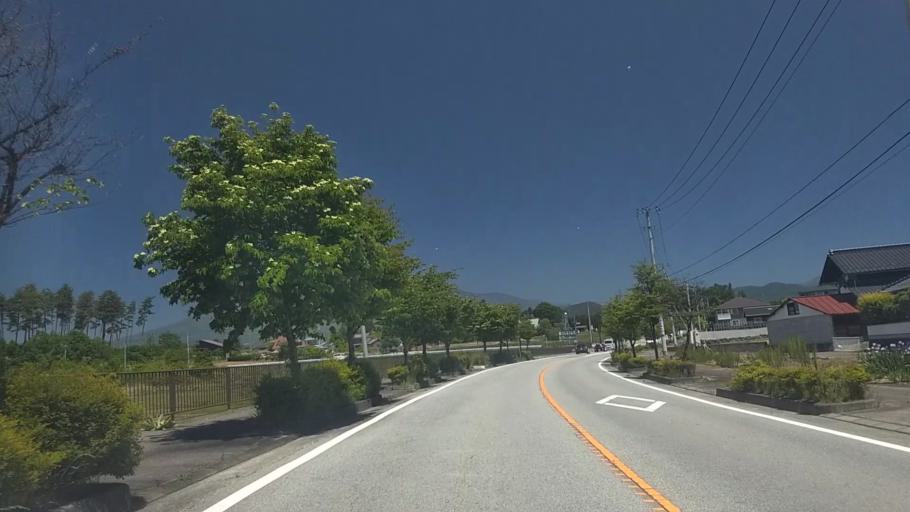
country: JP
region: Yamanashi
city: Nirasaki
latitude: 35.8144
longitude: 138.4291
